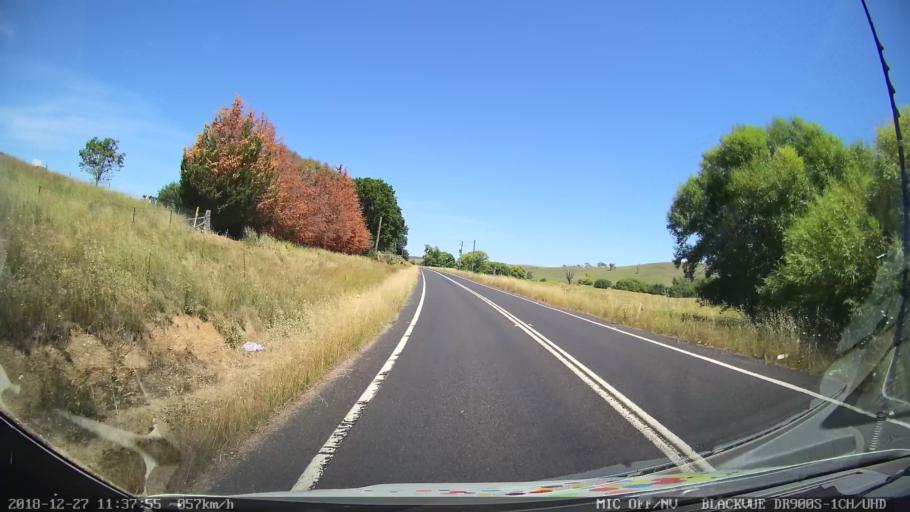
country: AU
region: New South Wales
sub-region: Bathurst Regional
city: Perthville
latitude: -33.5150
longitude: 149.5209
